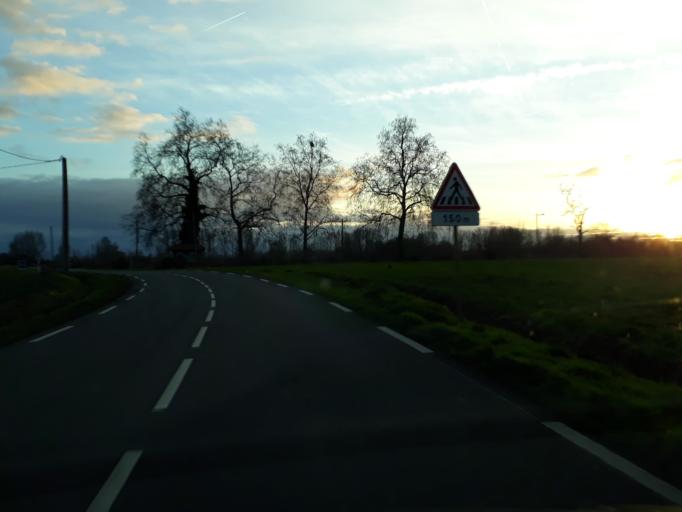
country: FR
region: Midi-Pyrenees
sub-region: Departement de la Haute-Garonne
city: Marquefave
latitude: 43.3296
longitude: 1.2478
